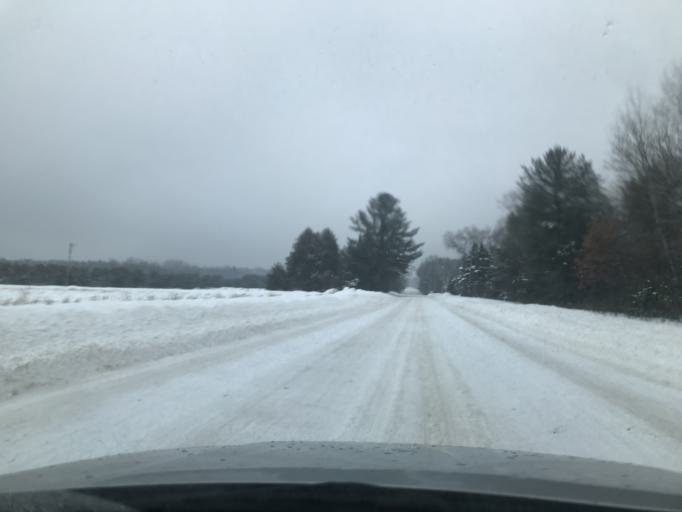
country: US
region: Wisconsin
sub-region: Marinette County
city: Peshtigo
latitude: 45.3812
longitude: -87.9380
